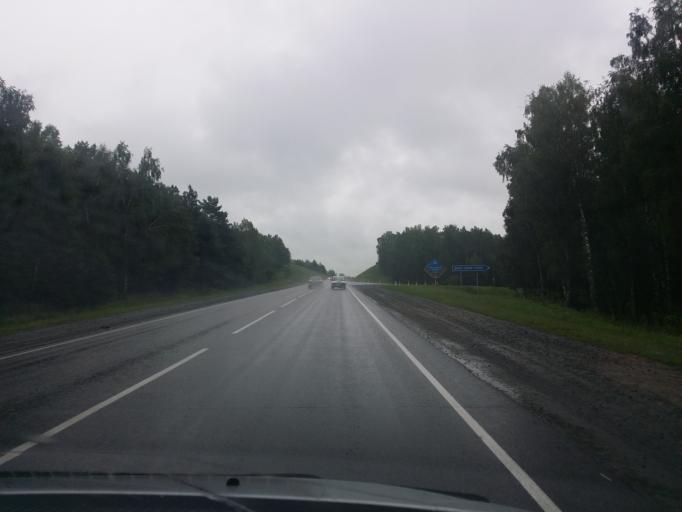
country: RU
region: Altai Krai
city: Bayunovskiye Klyuchi
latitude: 53.3394
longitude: 84.1549
